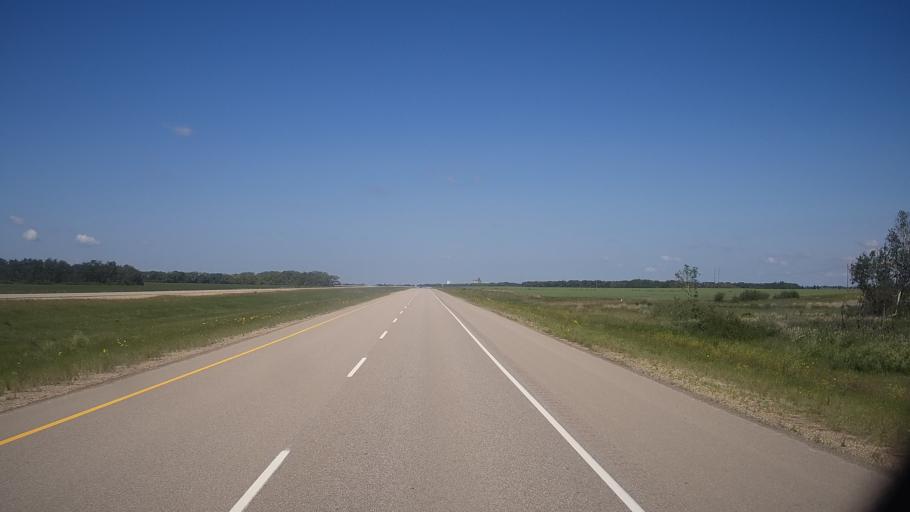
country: CA
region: Saskatchewan
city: Saskatoon
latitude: 52.0070
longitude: -106.3480
